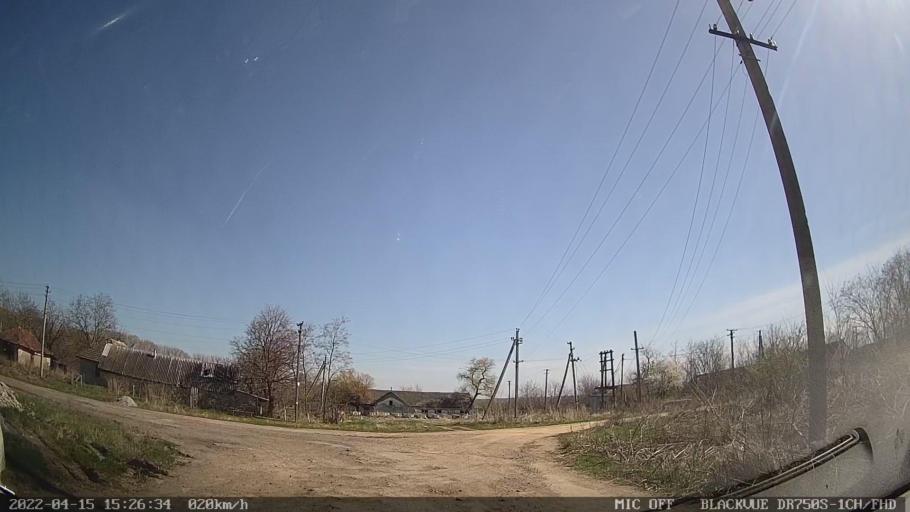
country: MD
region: Raionul Ocnita
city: Otaci
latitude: 48.3618
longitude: 27.9288
